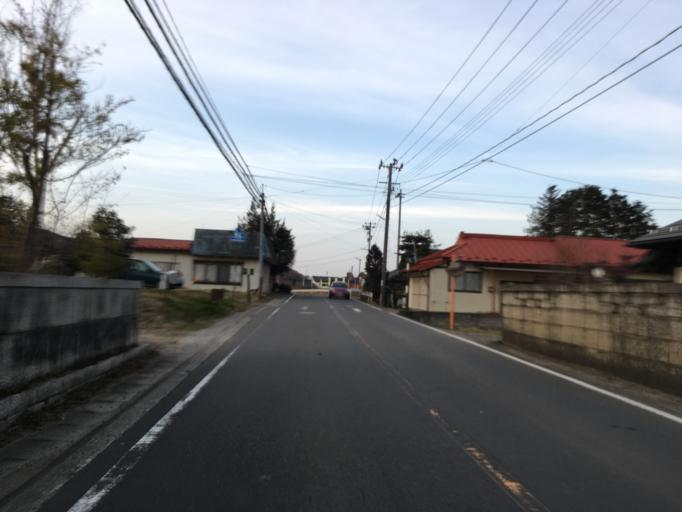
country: JP
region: Ibaraki
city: Daigo
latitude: 36.9332
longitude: 140.4086
